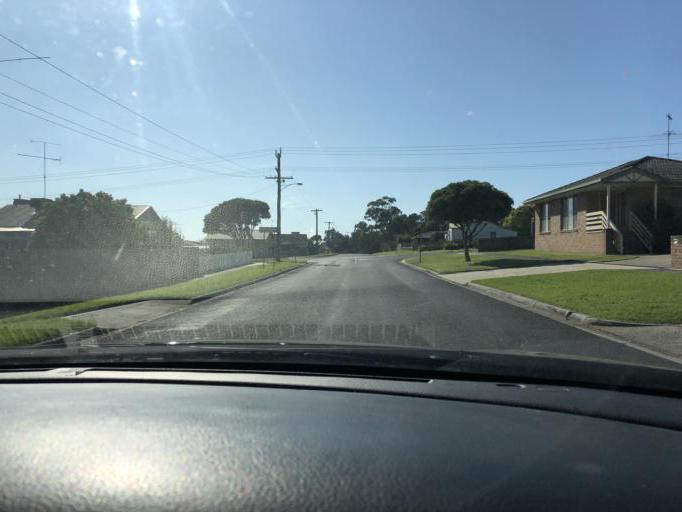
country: AU
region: Victoria
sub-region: Latrobe
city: Moe
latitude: -38.1839
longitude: 146.2609
